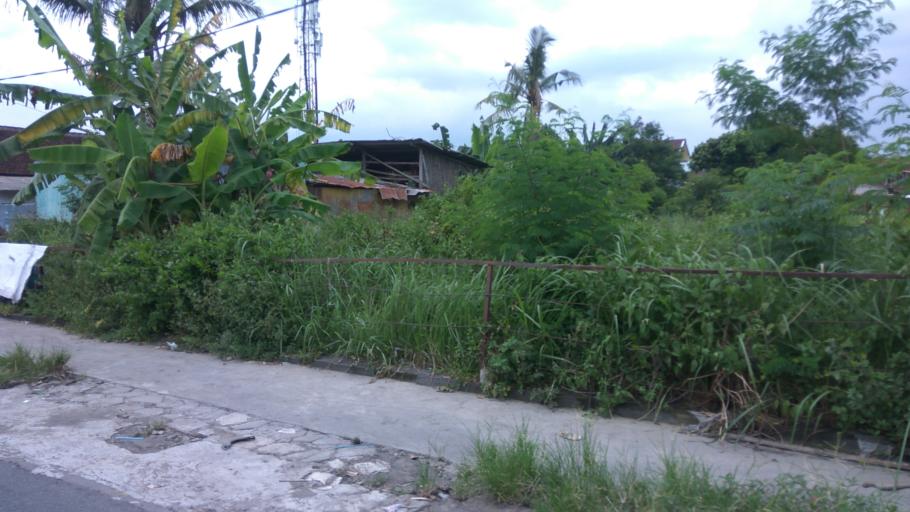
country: ID
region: Daerah Istimewa Yogyakarta
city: Depok
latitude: -7.7454
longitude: 110.4126
